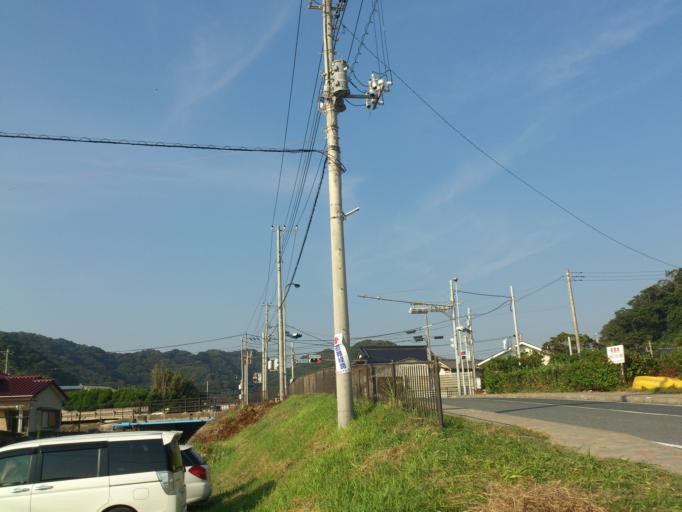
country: JP
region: Chiba
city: Tateyama
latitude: 35.0511
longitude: 139.8324
